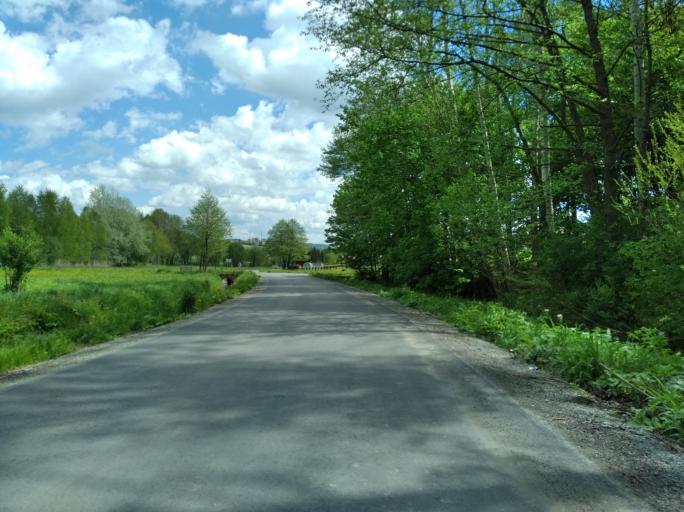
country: PL
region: Subcarpathian Voivodeship
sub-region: Powiat strzyzowski
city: Frysztak
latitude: 49.8304
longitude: 21.5872
